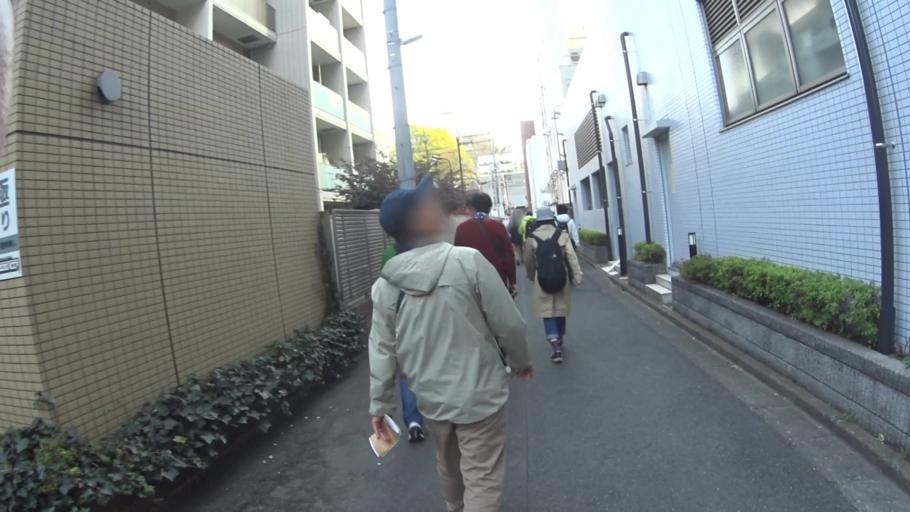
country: JP
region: Tokyo
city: Kokubunji
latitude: 35.7035
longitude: 139.5076
